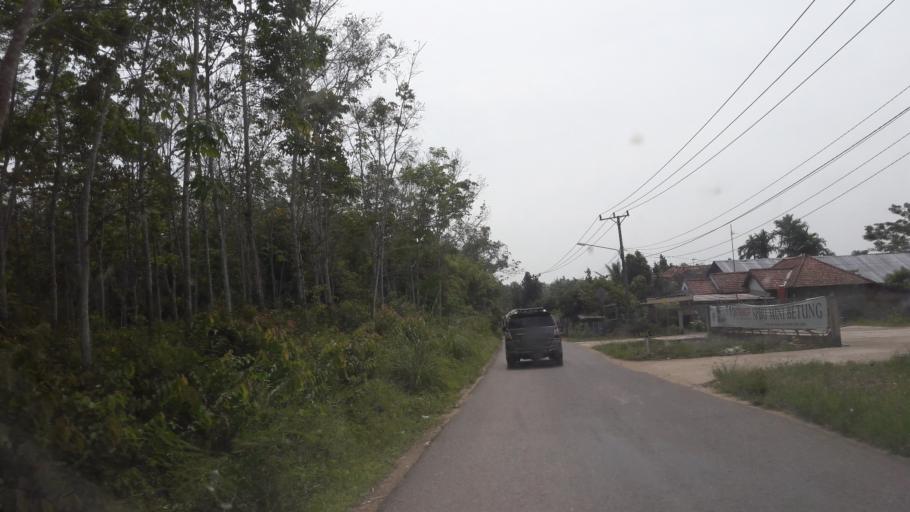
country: ID
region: South Sumatra
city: Gunungmenang
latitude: -3.1635
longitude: 104.1146
